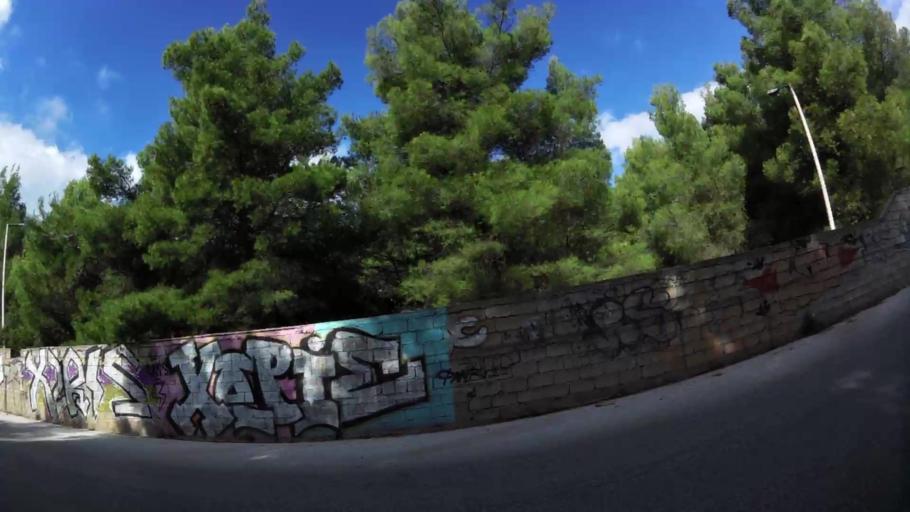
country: GR
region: Attica
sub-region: Nomarchia Athinas
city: Melissia
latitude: 38.0600
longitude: 23.8232
